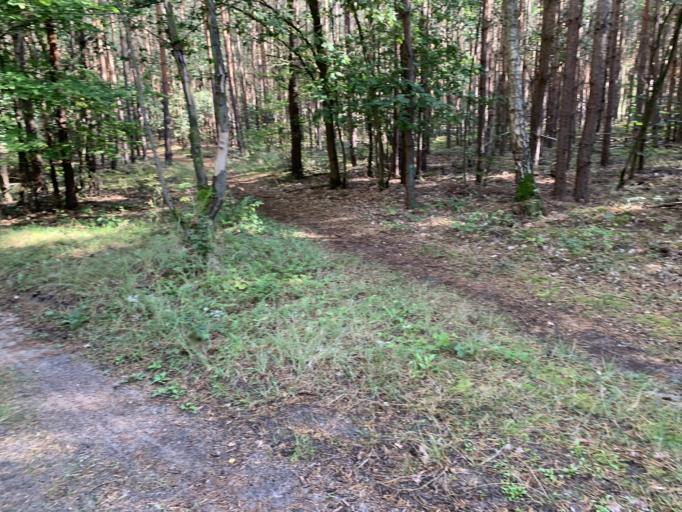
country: DE
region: Brandenburg
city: Wenzlow
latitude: 52.3493
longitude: 12.4856
